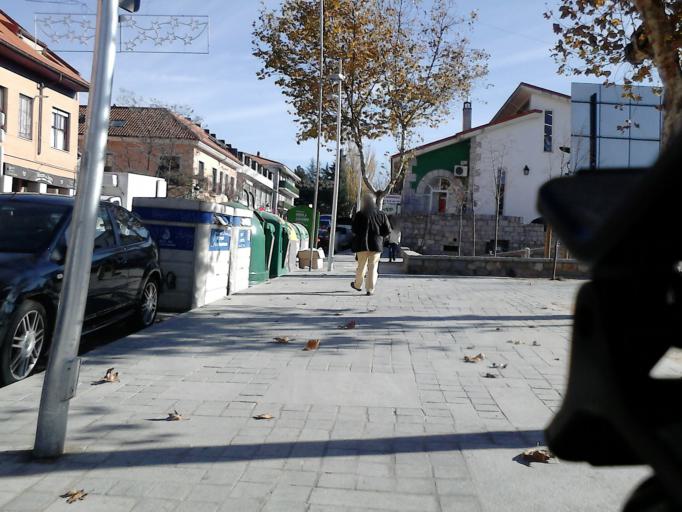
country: ES
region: Madrid
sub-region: Provincia de Madrid
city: Torrelodones
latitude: 40.5751
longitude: -3.9270
